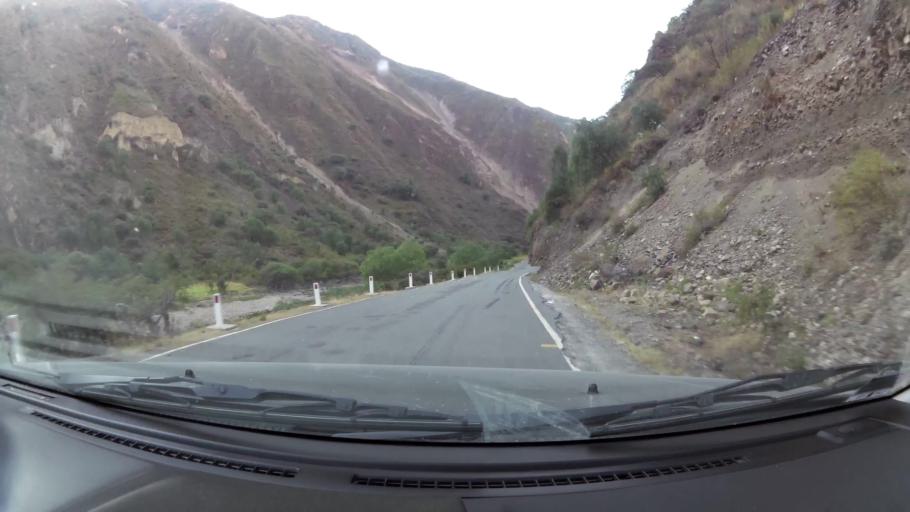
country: PE
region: Huancavelica
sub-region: Provincia de Churcampa
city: La Esmeralda
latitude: -12.5562
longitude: -74.7096
